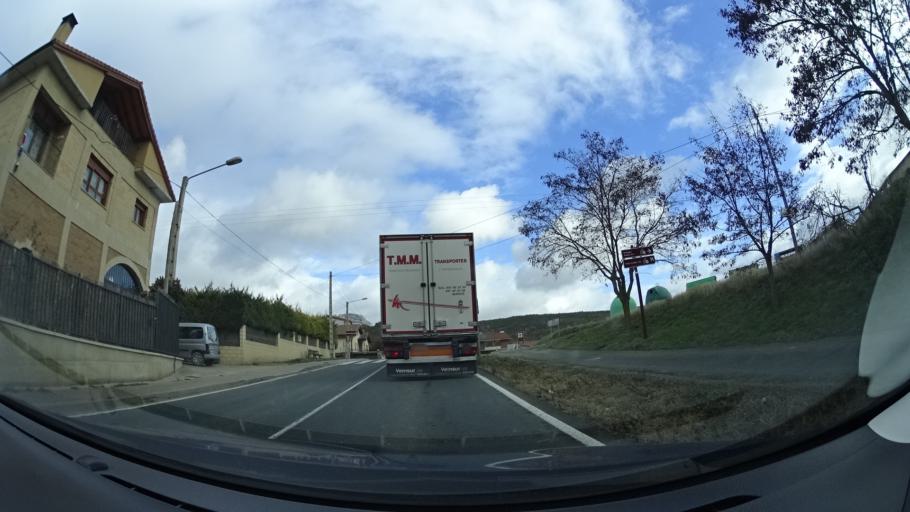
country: ES
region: La Rioja
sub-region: Provincia de La Rioja
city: Abalos
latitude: 42.5707
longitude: -2.7118
